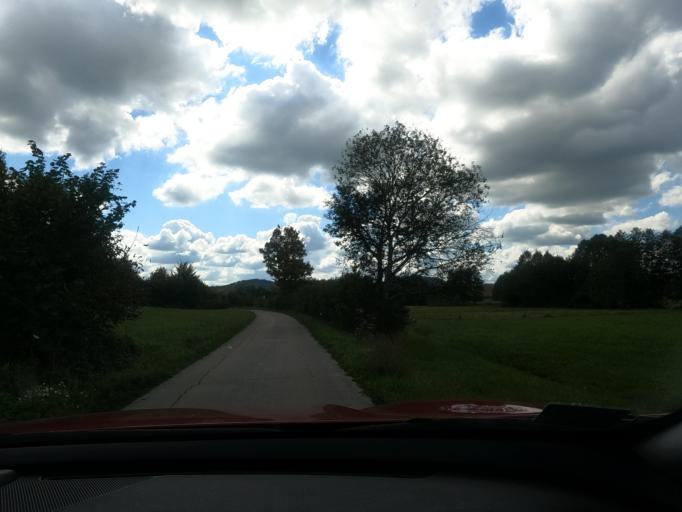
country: BA
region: Federation of Bosnia and Herzegovina
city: Velika Kladusa
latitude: 45.2196
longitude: 15.7104
